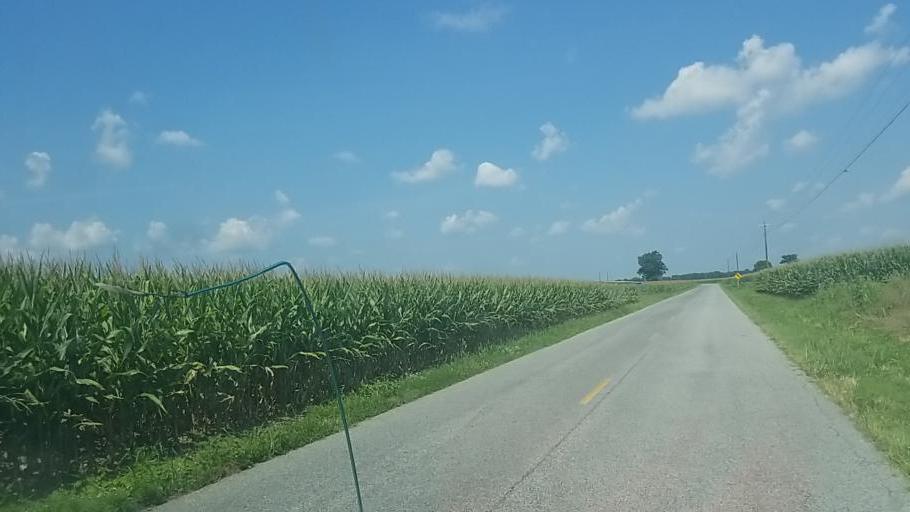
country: US
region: Maryland
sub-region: Worcester County
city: Berlin
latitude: 38.2917
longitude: -75.2456
